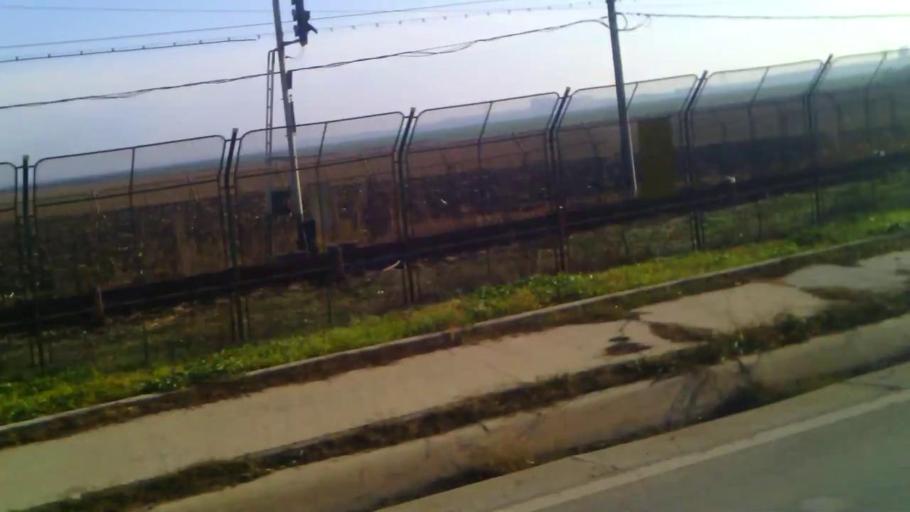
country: RO
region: Ilfov
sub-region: Comuna Popesti-Leordeni
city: Popesti-Leordeni
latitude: 44.3484
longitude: 26.1590
